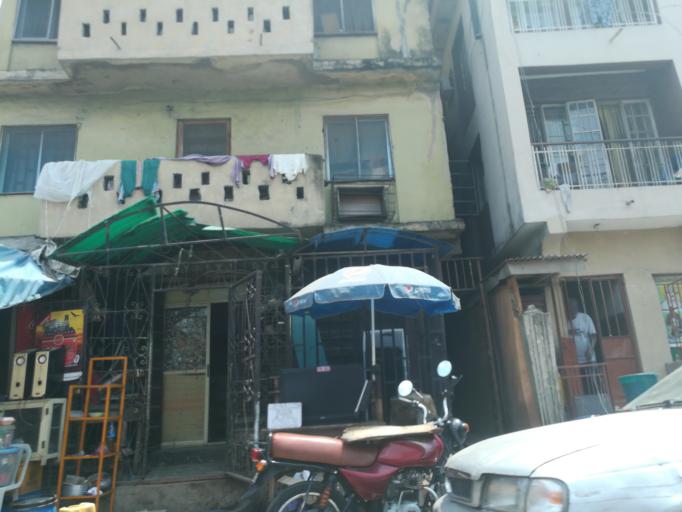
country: NG
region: Lagos
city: Lagos
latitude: 6.4530
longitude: 3.3966
